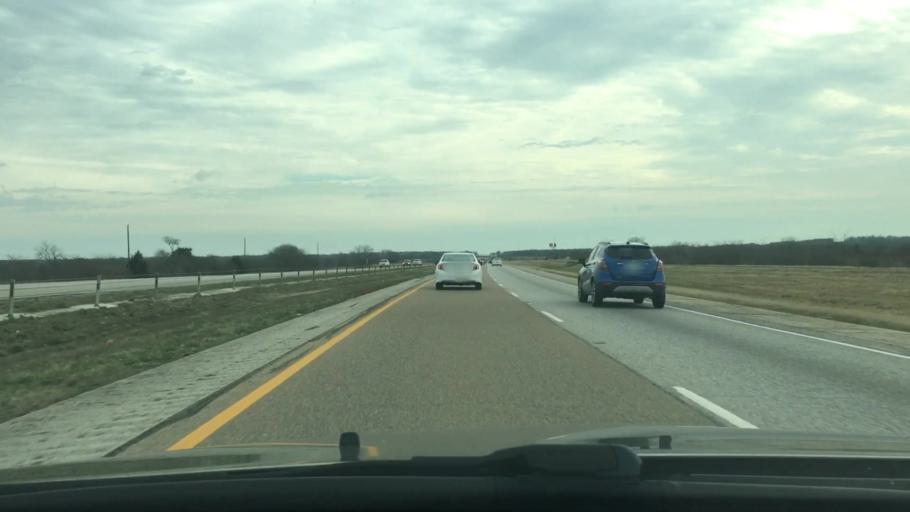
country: US
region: Texas
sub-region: Leon County
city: Centerville
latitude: 31.1041
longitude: -95.9651
